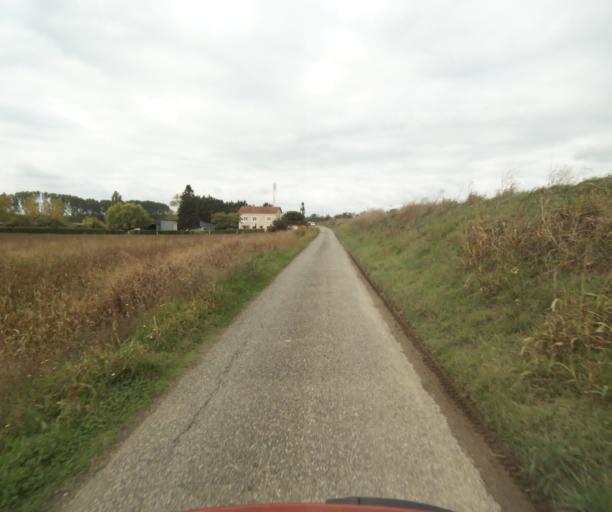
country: FR
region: Midi-Pyrenees
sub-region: Departement du Tarn-et-Garonne
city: Finhan
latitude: 43.8976
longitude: 1.2308
